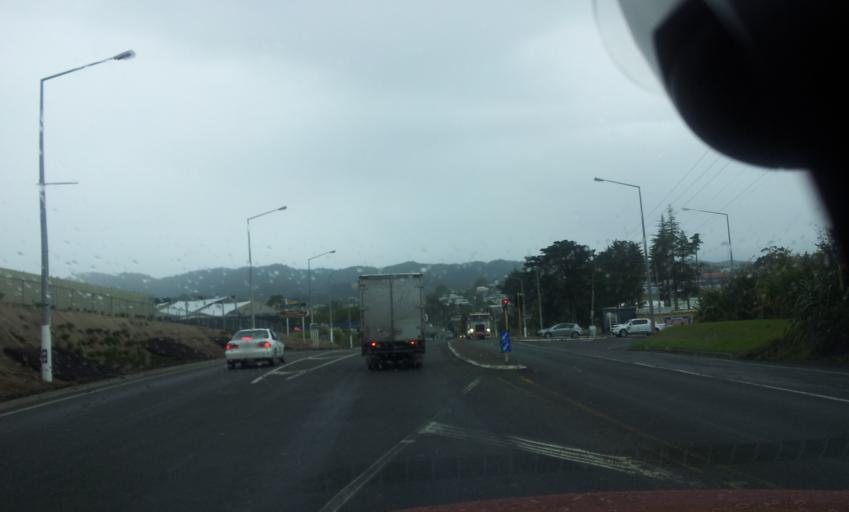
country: NZ
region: Northland
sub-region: Whangarei
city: Whangarei
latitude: -35.7532
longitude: 174.3100
